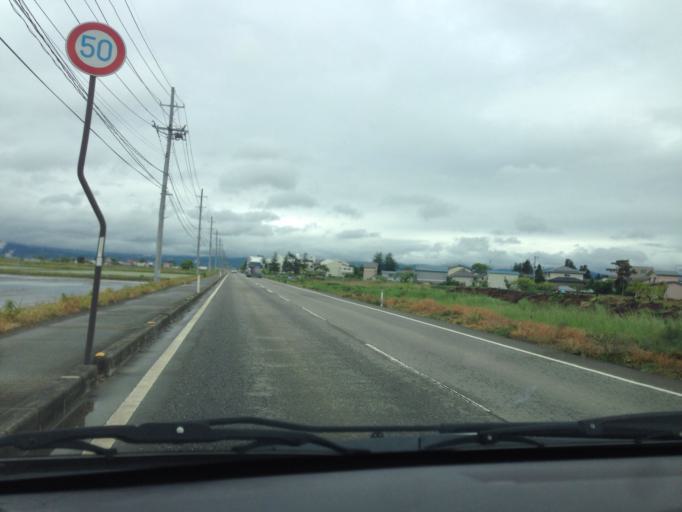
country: JP
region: Fukushima
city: Kitakata
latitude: 37.5525
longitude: 139.8393
